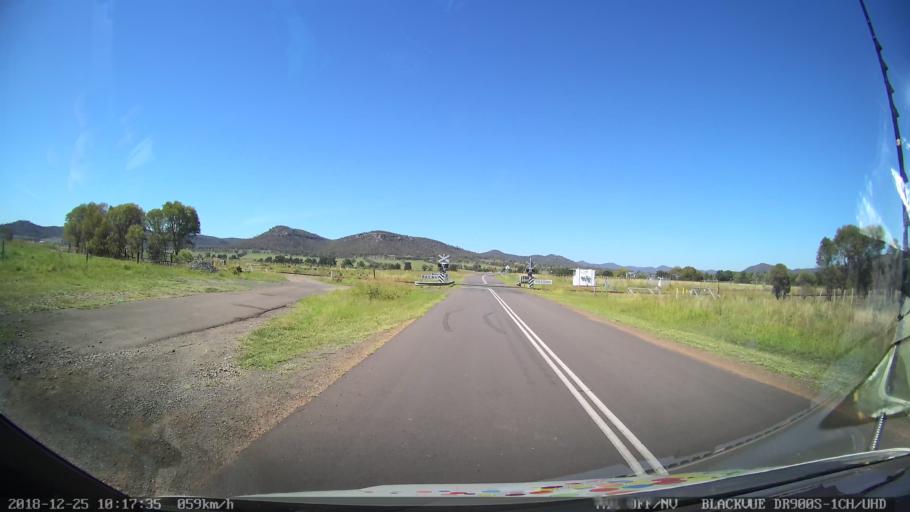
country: AU
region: New South Wales
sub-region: Muswellbrook
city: Denman
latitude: -32.3435
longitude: 150.5774
